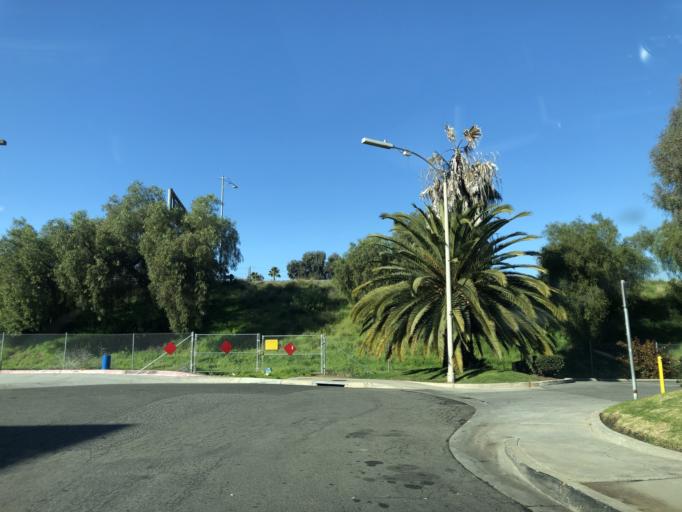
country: US
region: California
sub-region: San Diego County
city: Escondido
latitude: 33.1294
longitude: -117.0941
